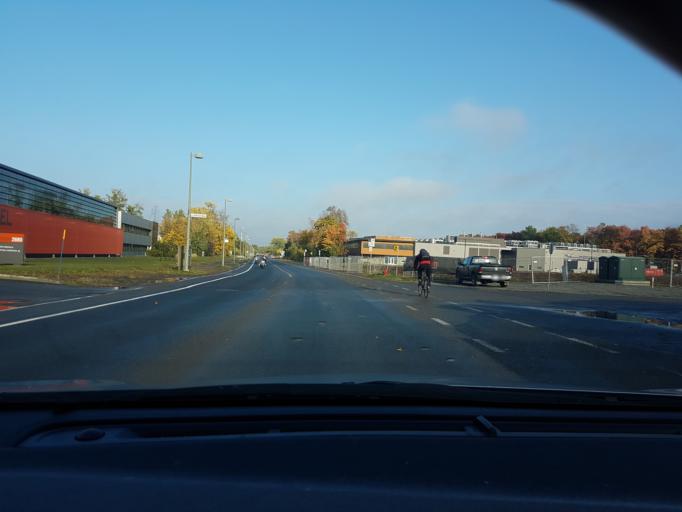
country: CA
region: Quebec
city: L'Ancienne-Lorette
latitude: 46.7963
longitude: -71.3086
